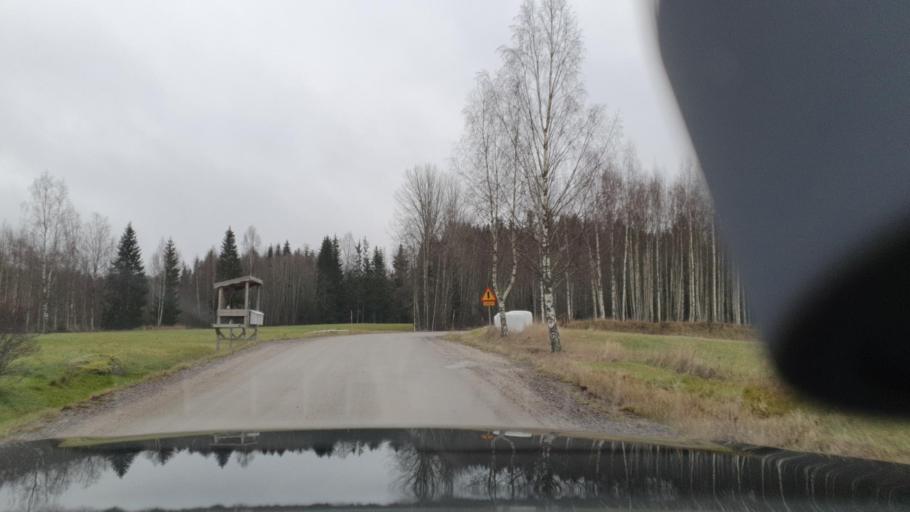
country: SE
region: Vaermland
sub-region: Eda Kommun
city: Amotfors
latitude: 59.7861
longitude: 12.3439
